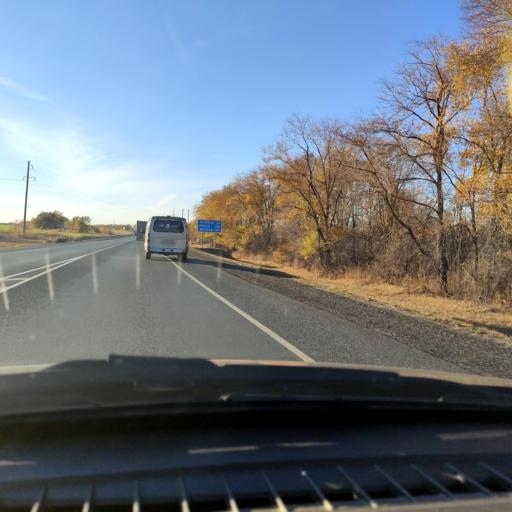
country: RU
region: Samara
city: Varlamovo
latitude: 53.1951
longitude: 48.3222
